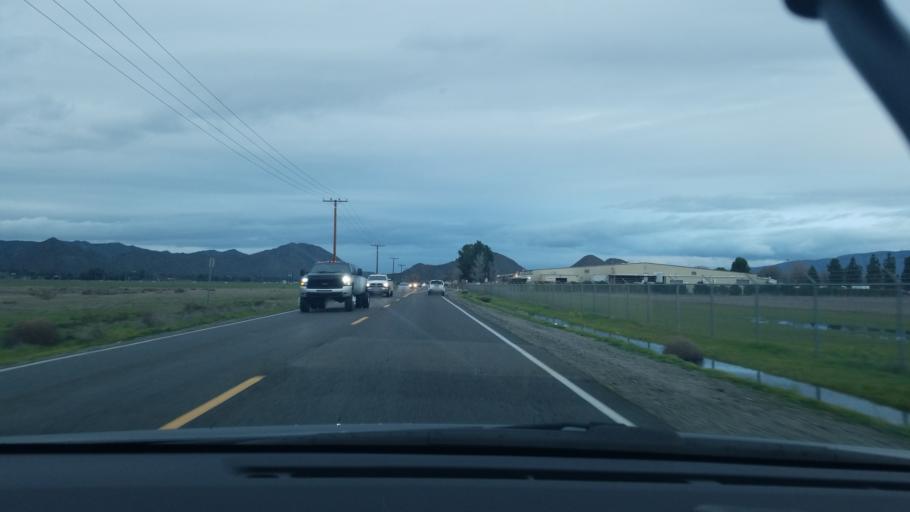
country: US
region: California
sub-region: Riverside County
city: Green Acres
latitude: 33.7330
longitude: -117.0327
